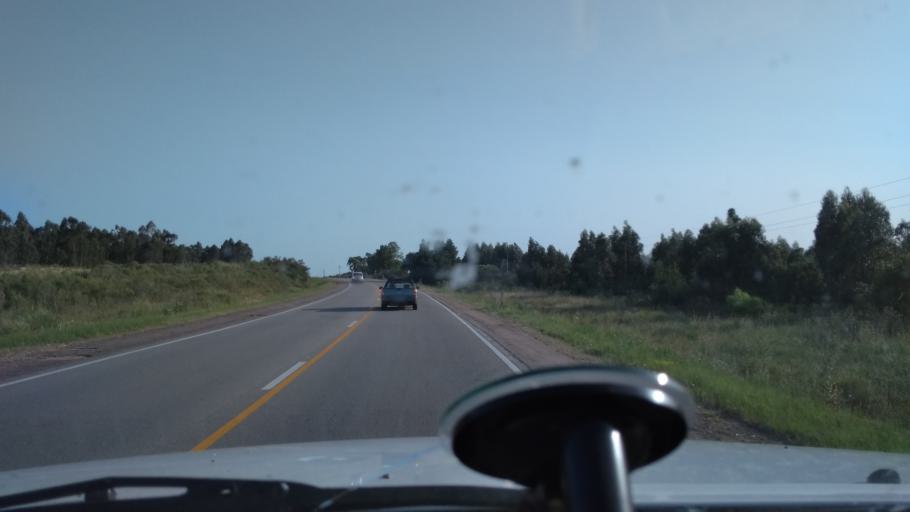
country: UY
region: Canelones
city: Sauce
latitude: -34.5777
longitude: -56.0571
